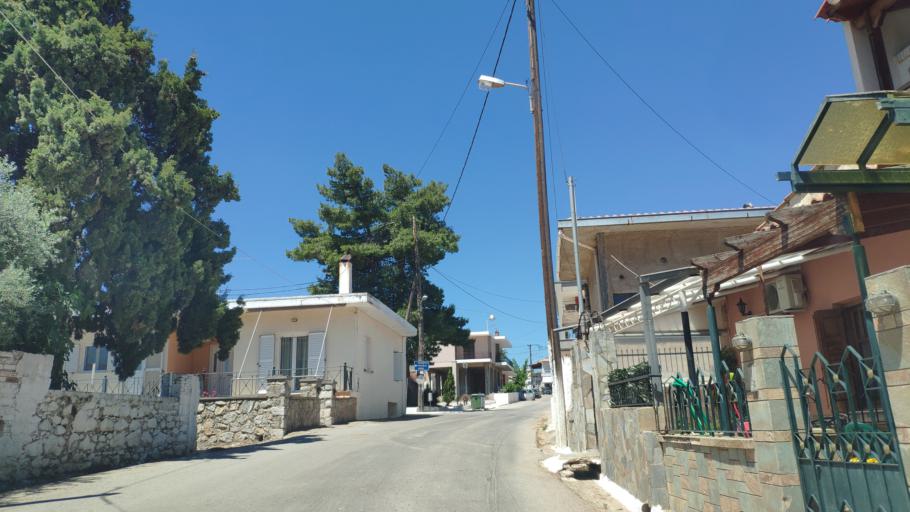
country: GR
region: Central Greece
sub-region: Nomos Voiotias
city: Kaparellion
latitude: 38.2661
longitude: 23.2367
